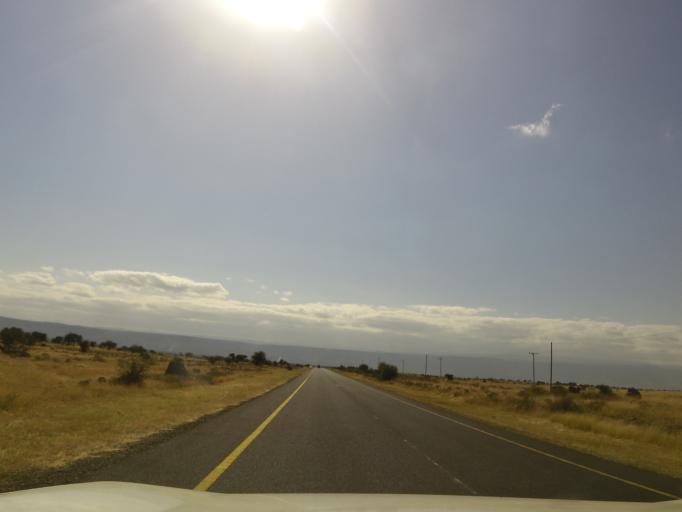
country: TZ
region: Arusha
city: Mto wa Mbu
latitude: -3.4000
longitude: 35.9094
